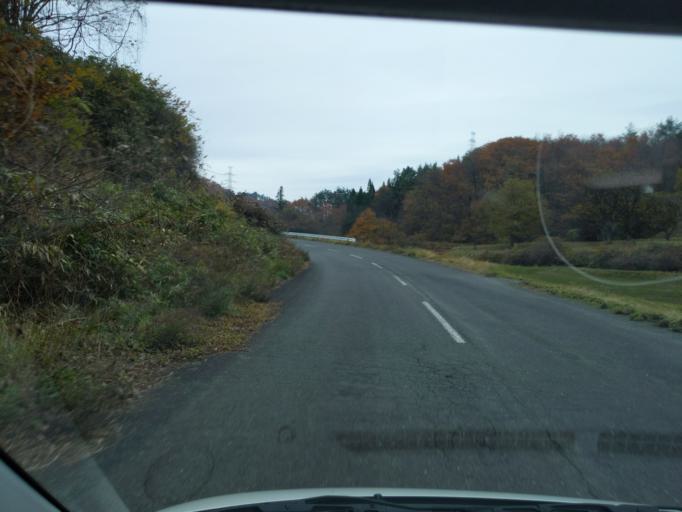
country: JP
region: Iwate
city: Ichinoseki
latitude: 39.0067
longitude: 141.0530
